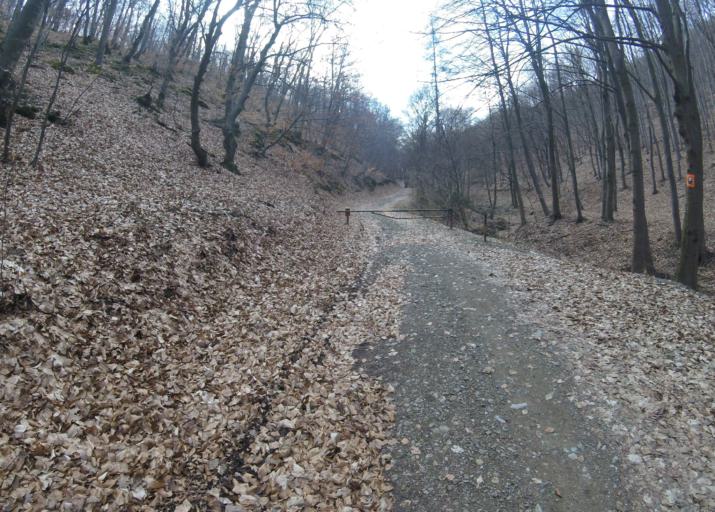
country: HU
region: Heves
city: Belapatfalva
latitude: 48.0369
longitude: 20.3532
